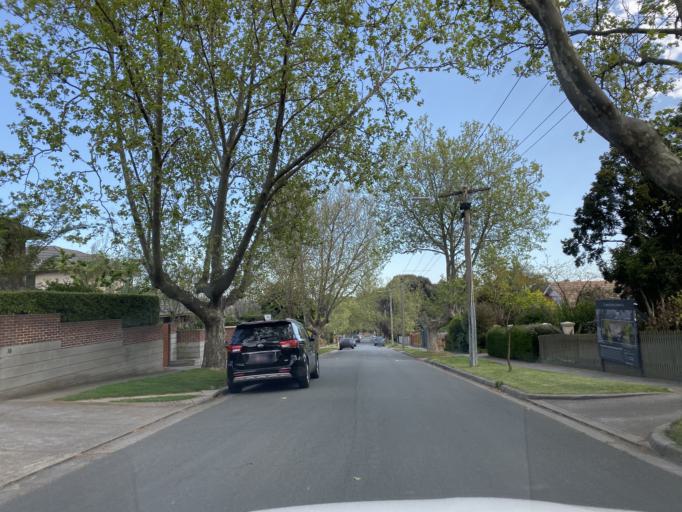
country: AU
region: Victoria
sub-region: Boroondara
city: Camberwell
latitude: -37.8351
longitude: 145.0787
